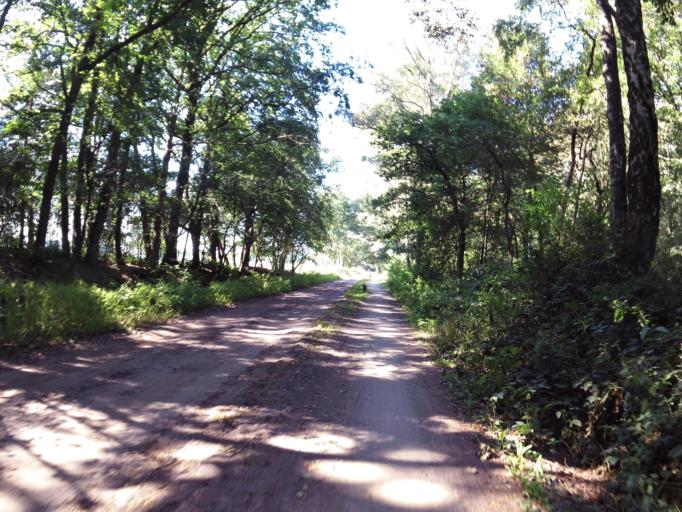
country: NL
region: Overijssel
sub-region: Gemeente Haaksbergen
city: Haaksbergen
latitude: 52.1513
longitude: 6.7964
